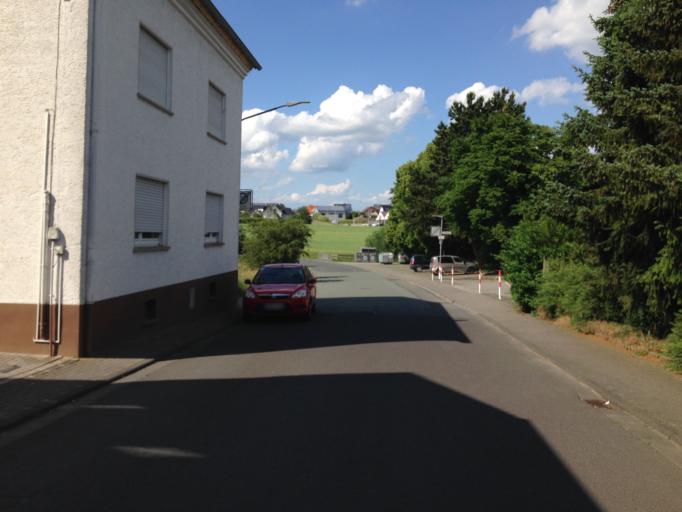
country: DE
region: Hesse
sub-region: Regierungsbezirk Giessen
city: Hoernsheim
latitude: 50.5149
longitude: 8.6190
